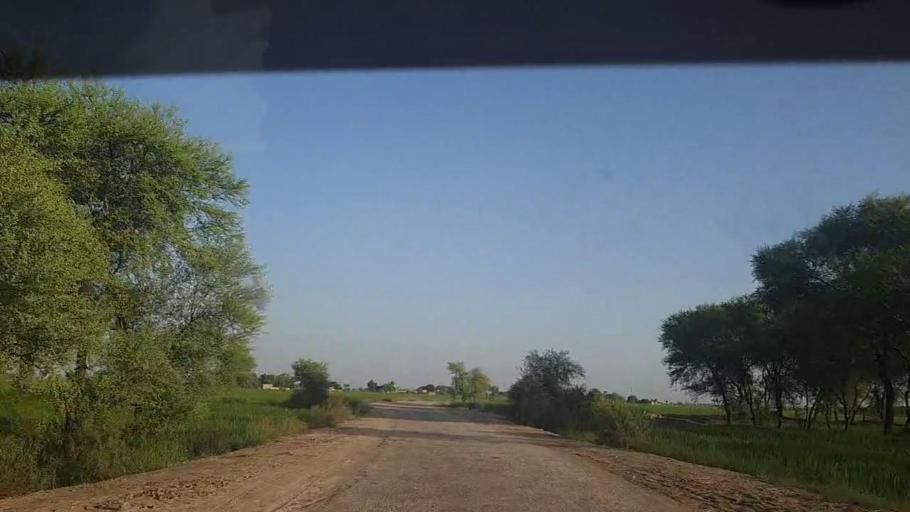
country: PK
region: Sindh
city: Thul
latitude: 28.2040
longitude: 68.8729
